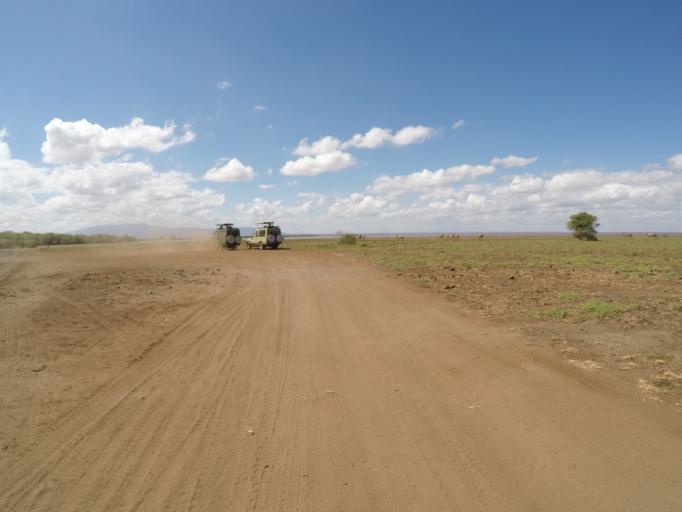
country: TZ
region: Arusha
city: Mto wa Mbu
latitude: -3.4269
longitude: 35.8163
